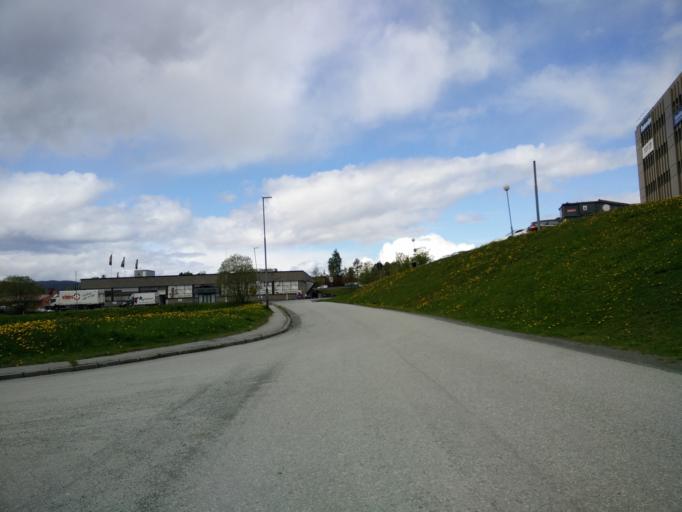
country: NO
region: Sor-Trondelag
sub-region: Trondheim
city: Trondheim
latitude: 63.4003
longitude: 10.4068
